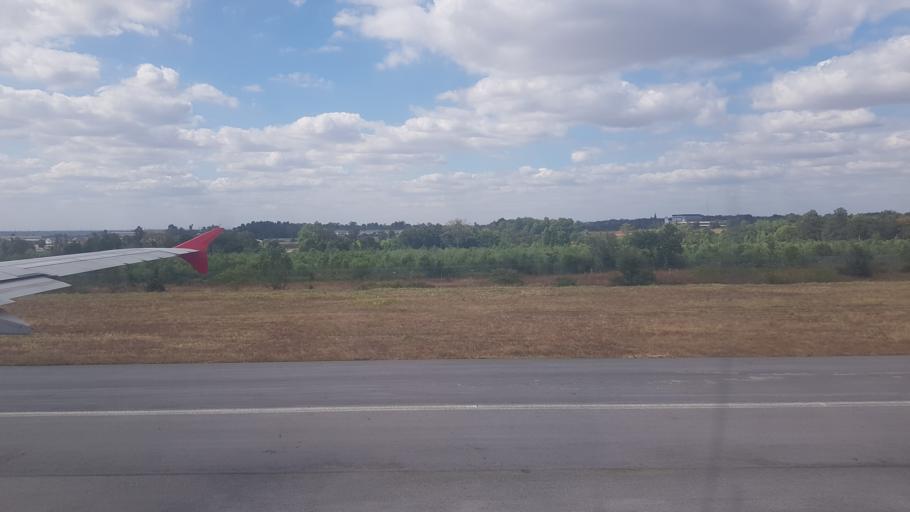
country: TH
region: Khon Kaen
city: Khon Kaen
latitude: 16.4618
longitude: 102.7805
